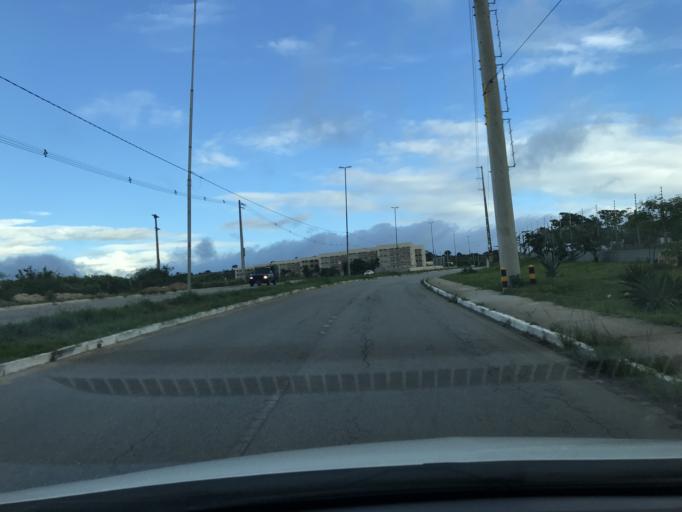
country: BR
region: Pernambuco
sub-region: Caruaru
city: Caruaru
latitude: -8.2995
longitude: -35.9396
